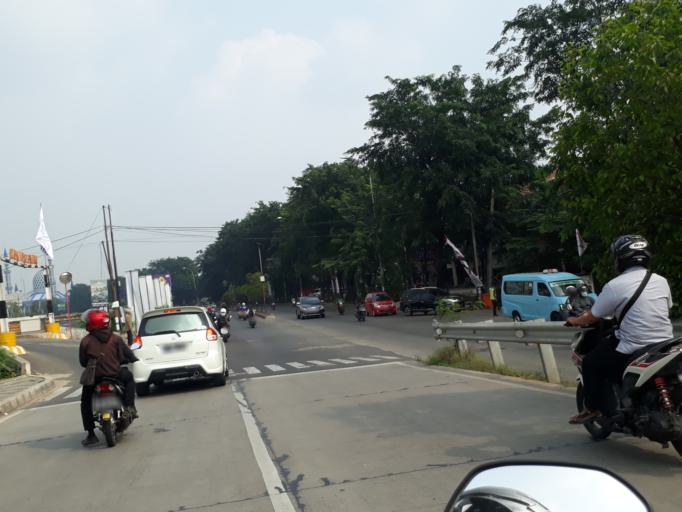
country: ID
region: West Java
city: Bekasi
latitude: -6.2477
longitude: 106.9781
